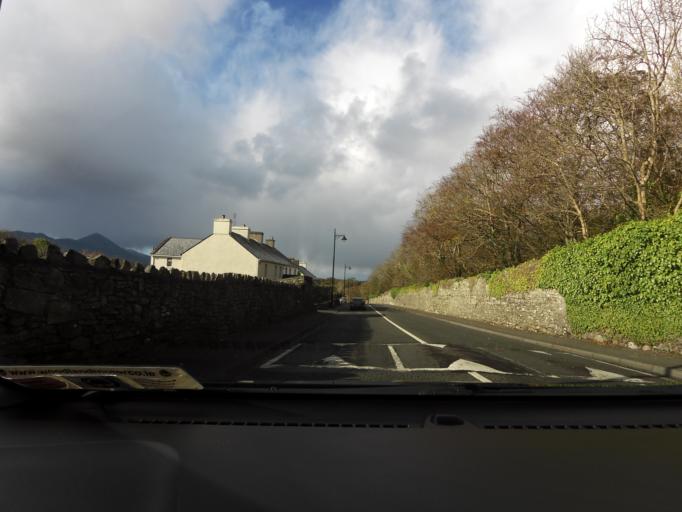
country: IE
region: Connaught
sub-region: Maigh Eo
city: Westport
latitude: 53.7984
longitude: -9.5354
